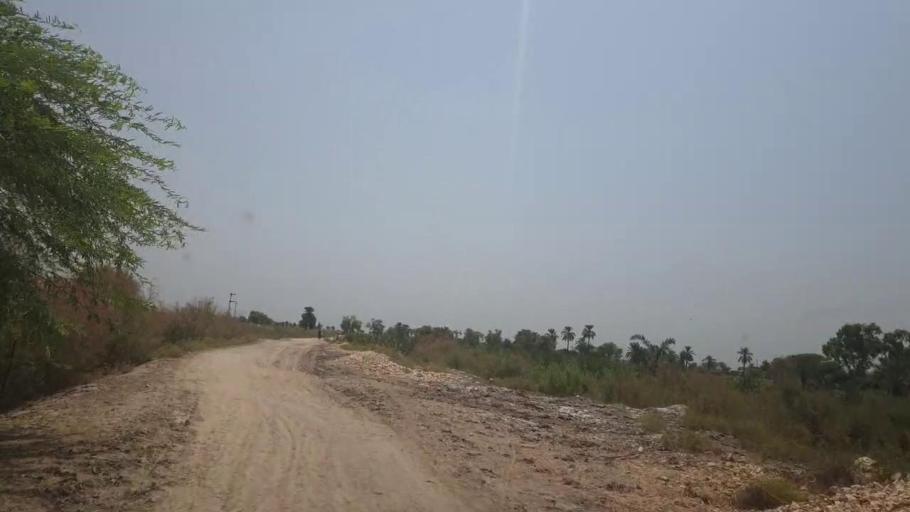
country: PK
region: Sindh
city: Lakhi
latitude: 27.8618
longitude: 68.6636
